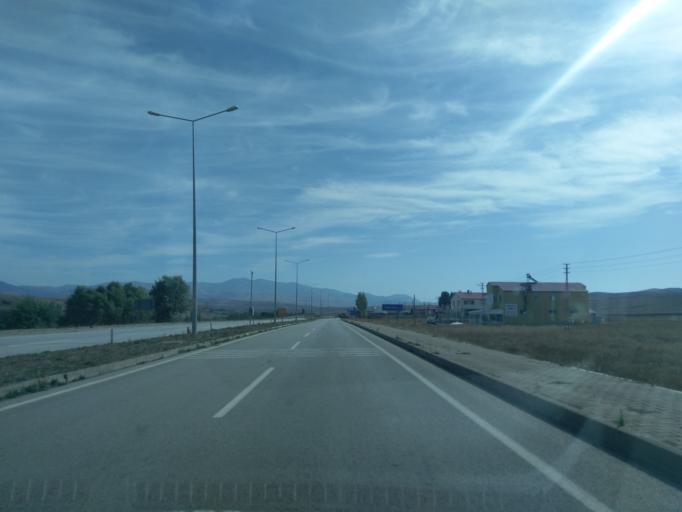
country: TR
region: Sivas
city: Imranli
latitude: 39.8709
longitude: 38.1315
